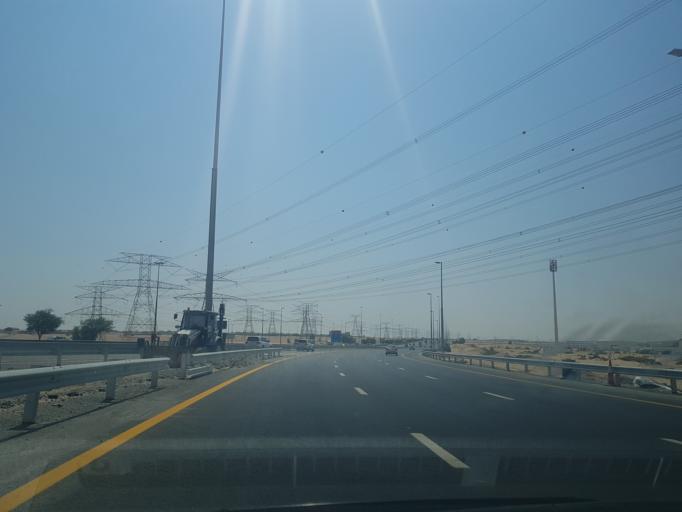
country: AE
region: Ash Shariqah
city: Sharjah
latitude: 25.2343
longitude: 55.5642
